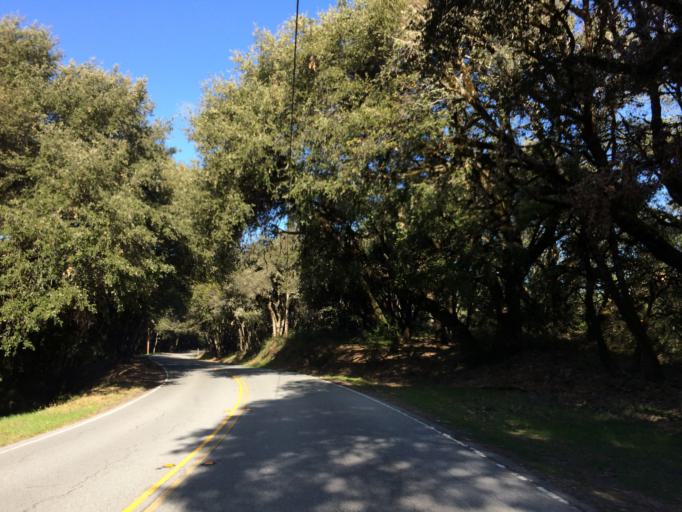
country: US
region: California
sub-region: Santa Clara County
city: Loyola
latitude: 37.2657
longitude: -122.1357
